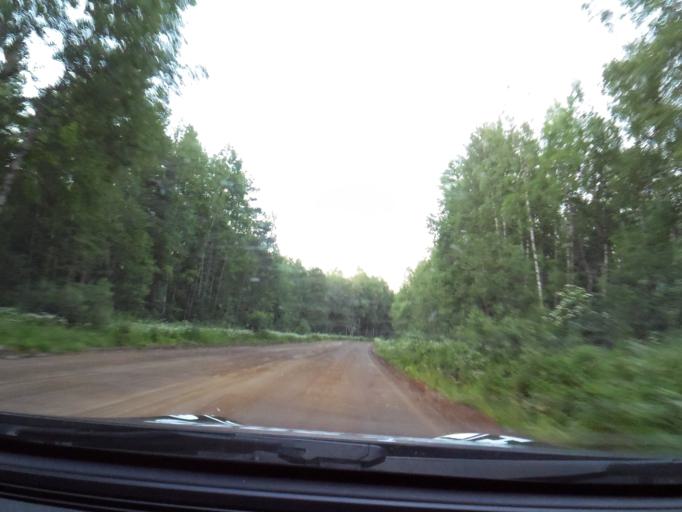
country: RU
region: Leningrad
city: Voznesen'ye
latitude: 60.8544
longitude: 35.8819
